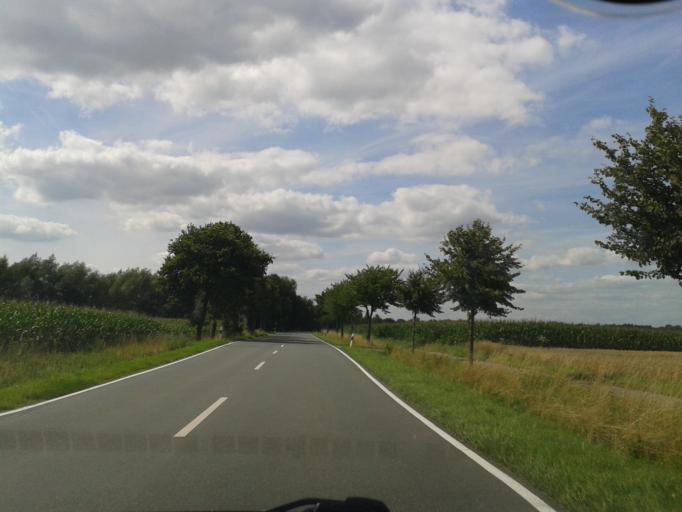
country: DE
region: North Rhine-Westphalia
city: Bad Lippspringe
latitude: 51.7607
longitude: 8.8121
